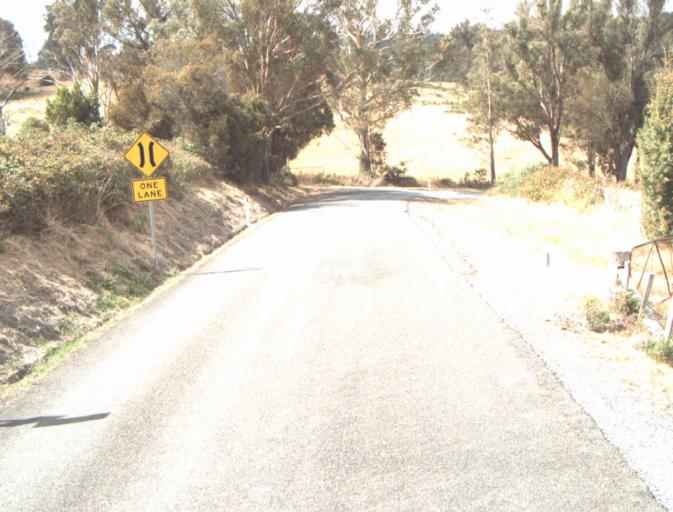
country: AU
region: Tasmania
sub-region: Launceston
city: Mayfield
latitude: -41.3113
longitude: 147.0453
